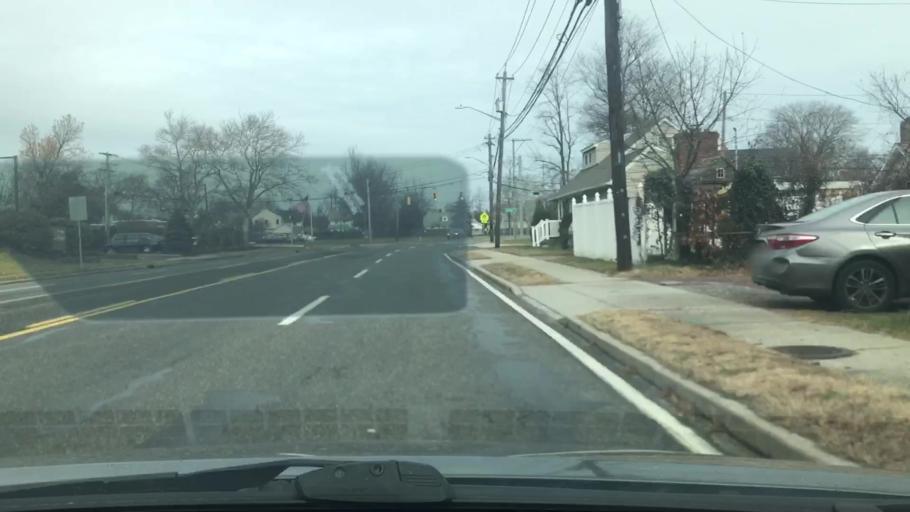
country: US
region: New York
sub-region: Suffolk County
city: Babylon
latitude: 40.6908
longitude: -73.3450
